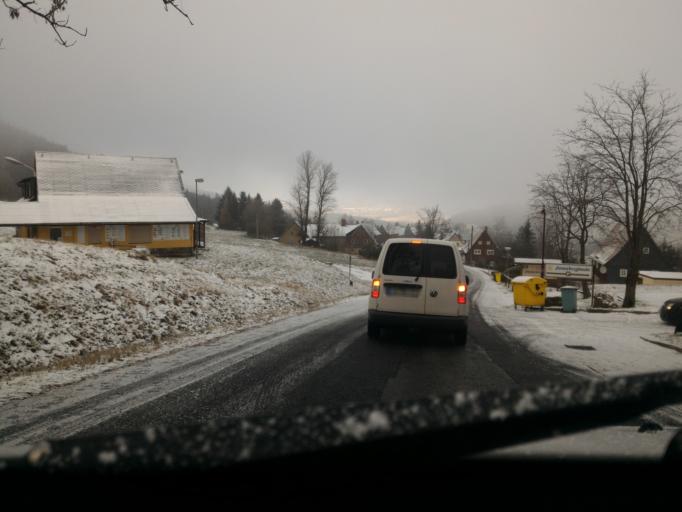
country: DE
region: Saxony
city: Kurort Jonsdorf
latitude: 50.8531
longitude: 14.6555
